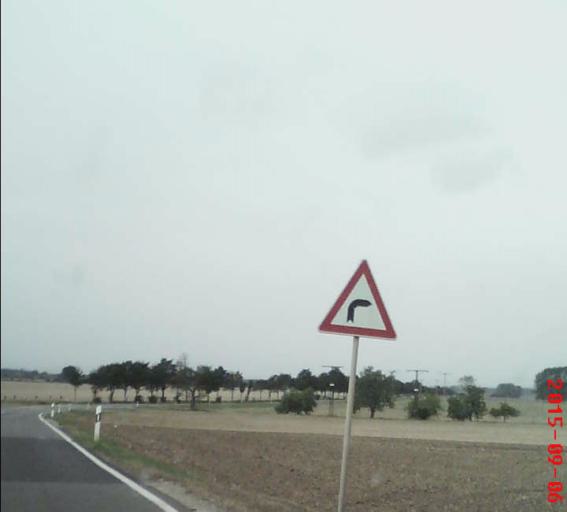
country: DE
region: Thuringia
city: Altengottern
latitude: 51.1520
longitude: 10.5543
